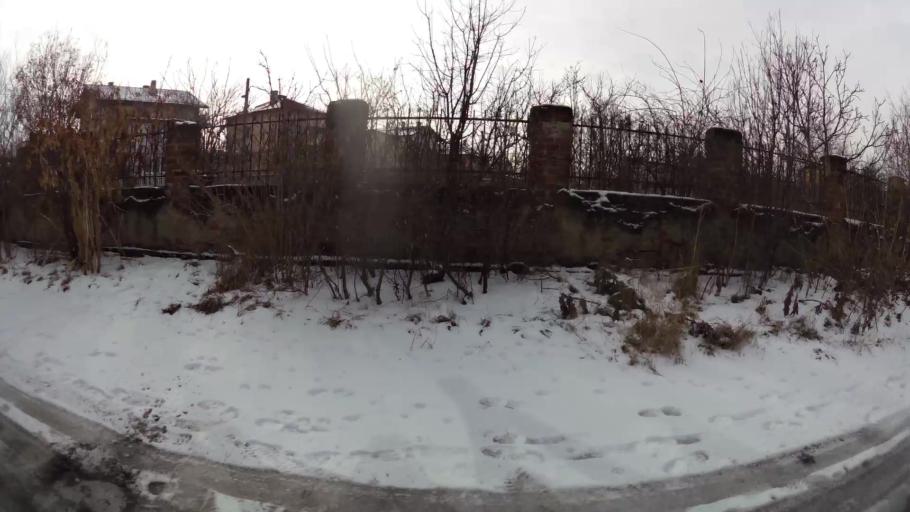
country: BG
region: Sofia-Capital
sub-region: Stolichna Obshtina
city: Sofia
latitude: 42.7144
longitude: 23.4080
